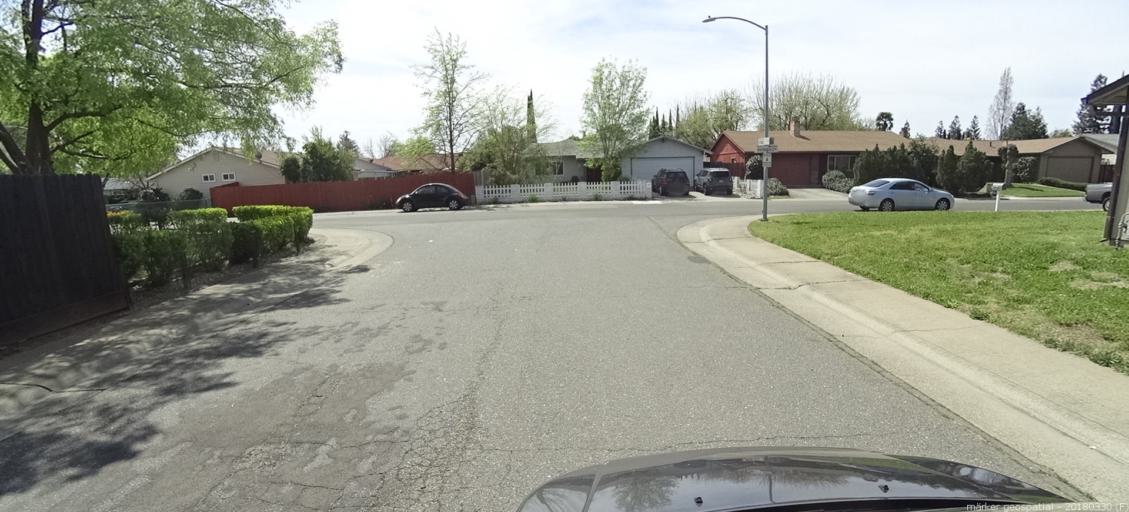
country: US
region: California
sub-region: Sacramento County
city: Rosemont
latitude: 38.5432
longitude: -121.3689
